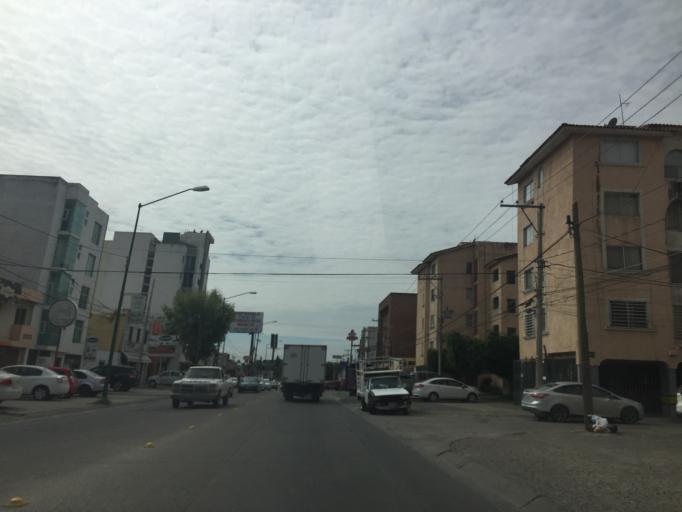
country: MX
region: Guanajuato
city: Leon
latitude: 21.1585
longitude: -101.6837
